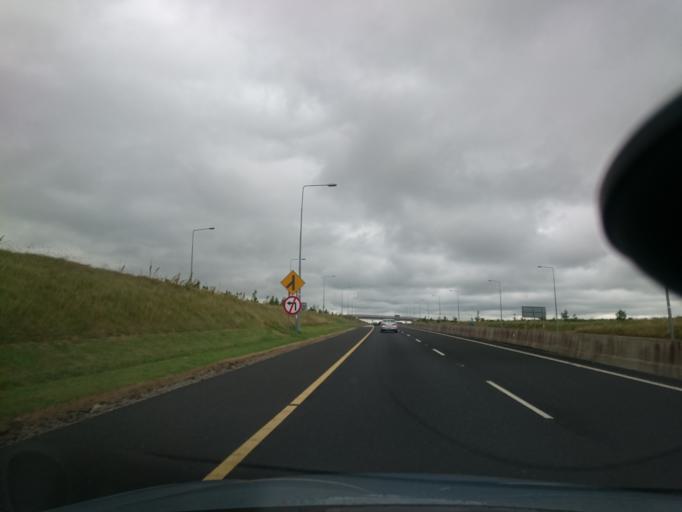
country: IE
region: Leinster
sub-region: Kildare
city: Moone
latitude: 52.9998
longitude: -6.8420
